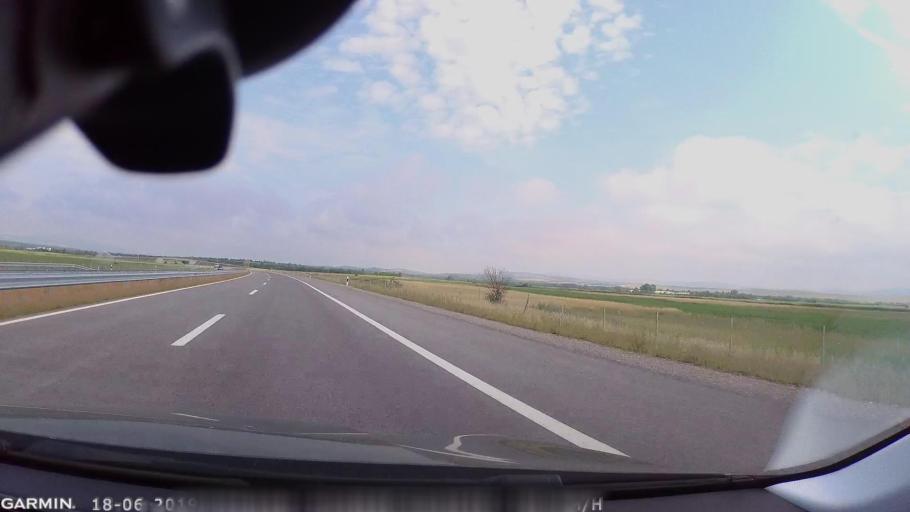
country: MK
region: Sveti Nikole
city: Sveti Nikole
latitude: 41.8216
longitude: 22.0133
